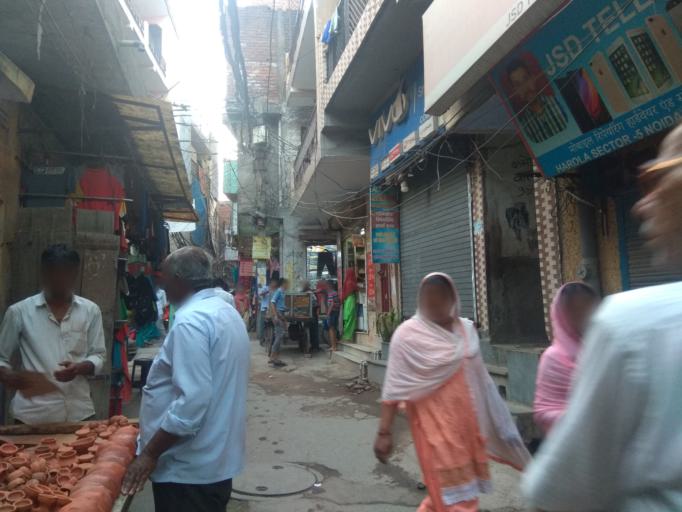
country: IN
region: Uttar Pradesh
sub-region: Gautam Buddha Nagar
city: Noida
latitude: 28.5878
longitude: 77.3208
